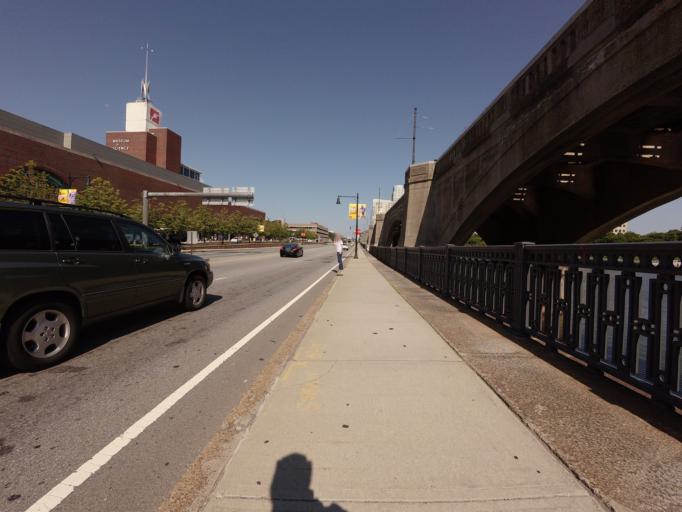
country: US
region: Massachusetts
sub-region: Suffolk County
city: Boston
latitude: 42.3675
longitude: -71.0695
